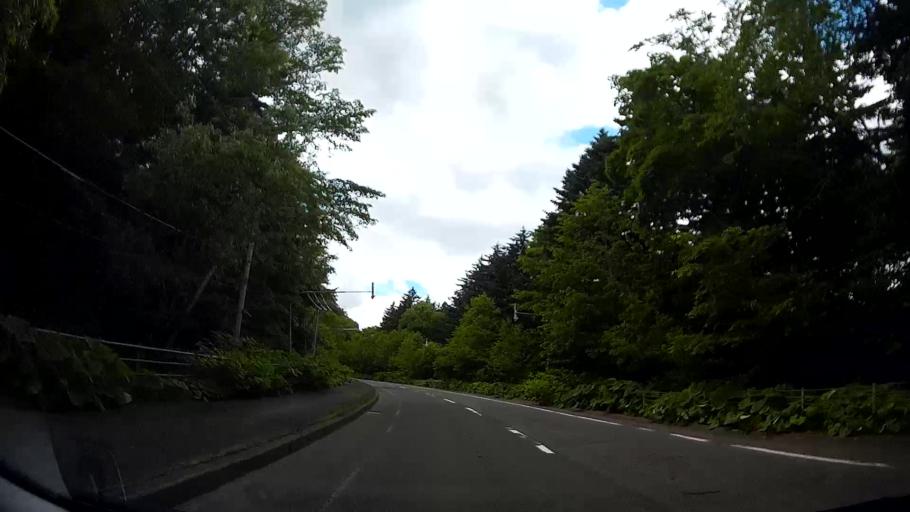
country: JP
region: Hokkaido
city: Kitahiroshima
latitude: 42.8451
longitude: 141.4592
